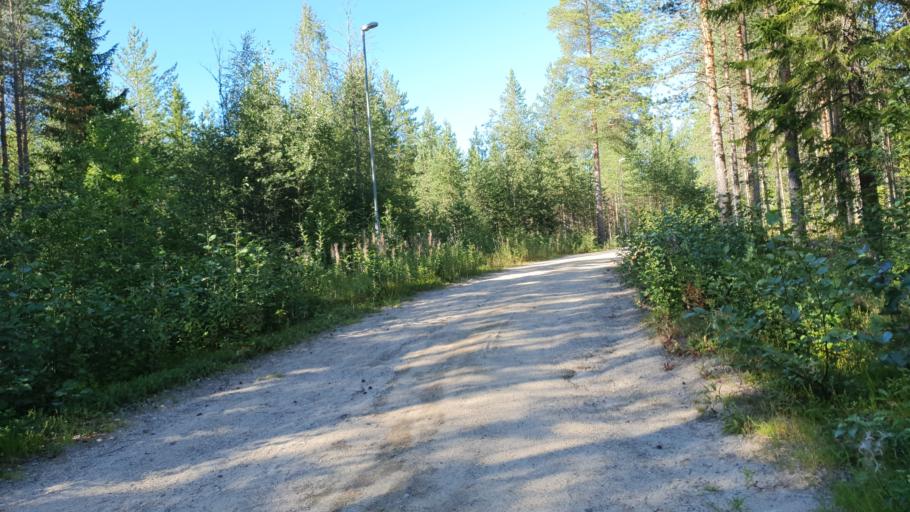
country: FI
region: Kainuu
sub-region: Kehys-Kainuu
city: Kuhmo
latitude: 64.1111
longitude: 29.5092
